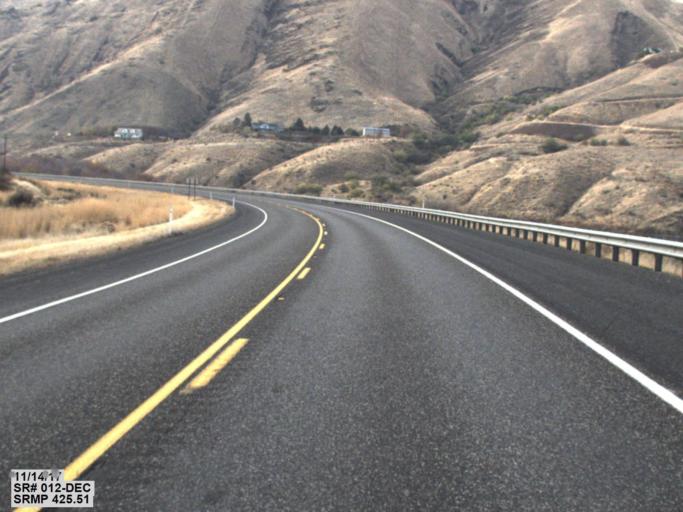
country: US
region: Washington
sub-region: Asotin County
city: Clarkston Heights-Vineland
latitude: 46.4149
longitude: -117.2047
